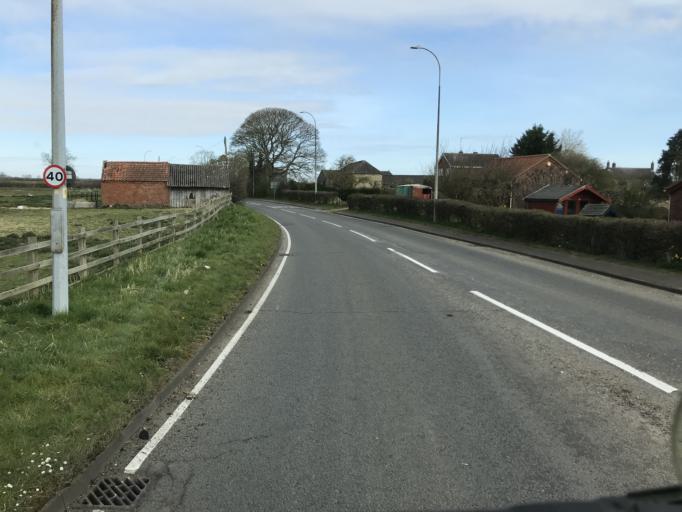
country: GB
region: England
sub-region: Lincolnshire
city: Market Rasen
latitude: 53.3897
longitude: -0.4043
